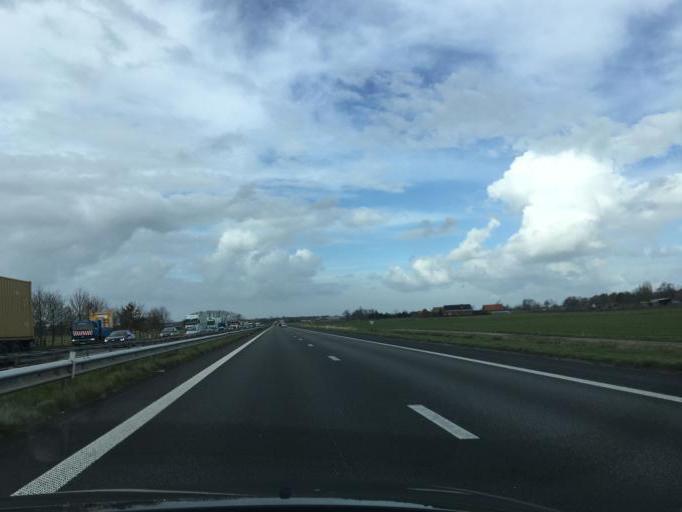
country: BE
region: Flanders
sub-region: Provincie West-Vlaanderen
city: Lichtervelde
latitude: 51.0457
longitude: 3.1619
